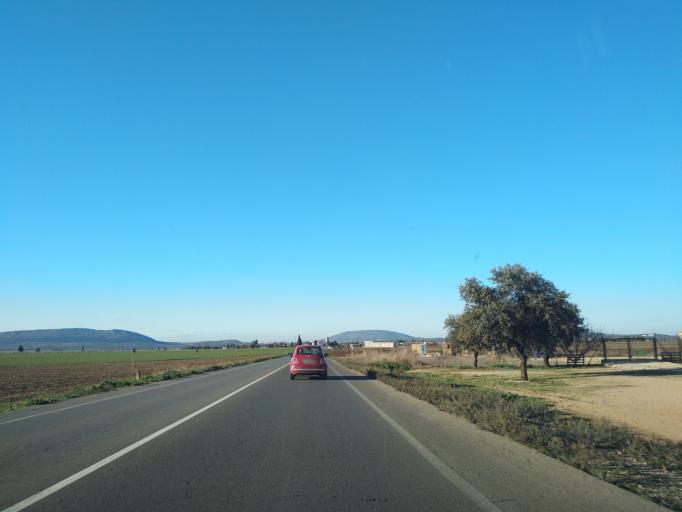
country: ES
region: Andalusia
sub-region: Provincia de Malaga
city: Antequera
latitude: 37.0608
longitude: -4.5940
